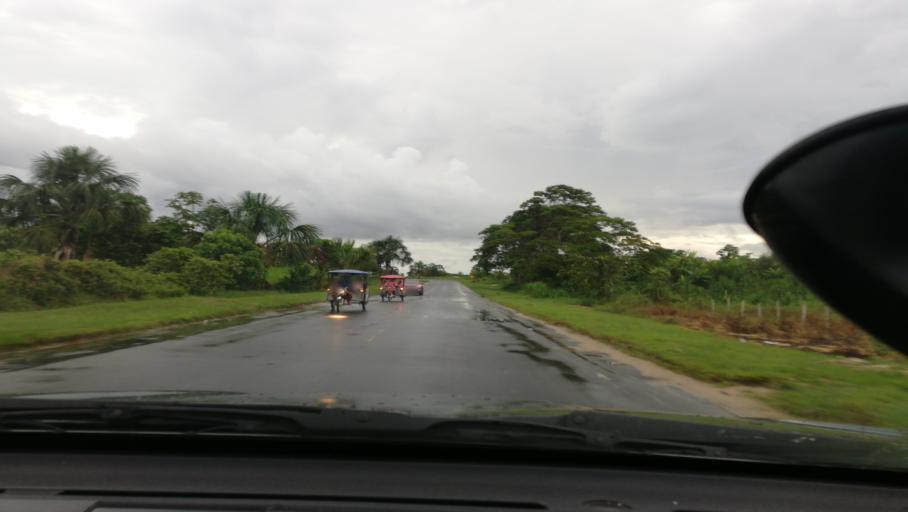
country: PE
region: Loreto
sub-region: Provincia de Maynas
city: San Juan
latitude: -3.9176
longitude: -73.3672
